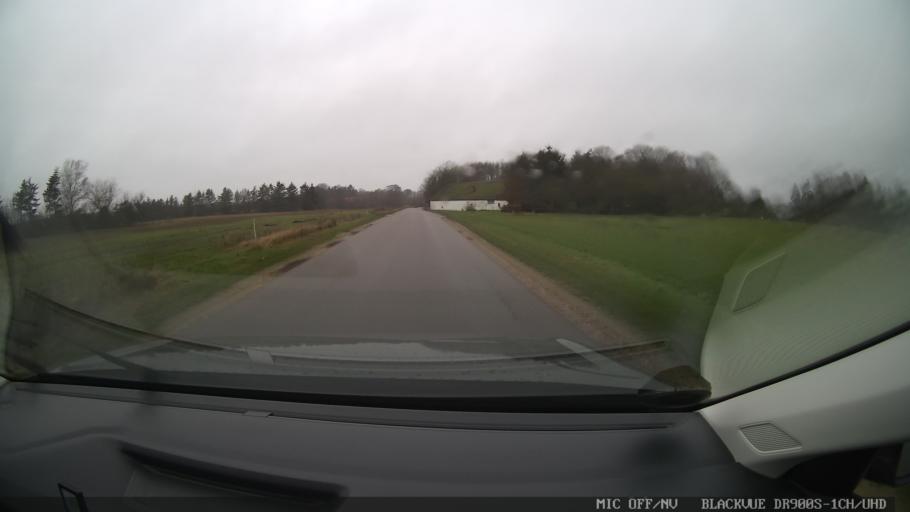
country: DK
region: Central Jutland
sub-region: Viborg Kommune
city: Karup
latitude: 56.2875
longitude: 9.1671
